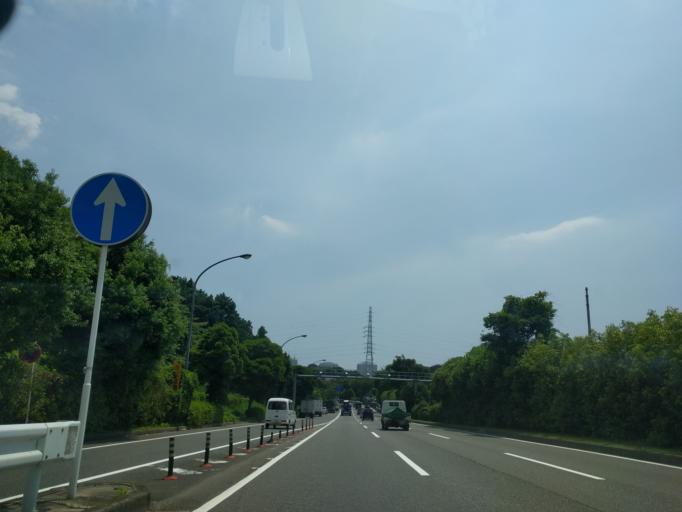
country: JP
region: Kanagawa
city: Yokohama
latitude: 35.4407
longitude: 139.5604
